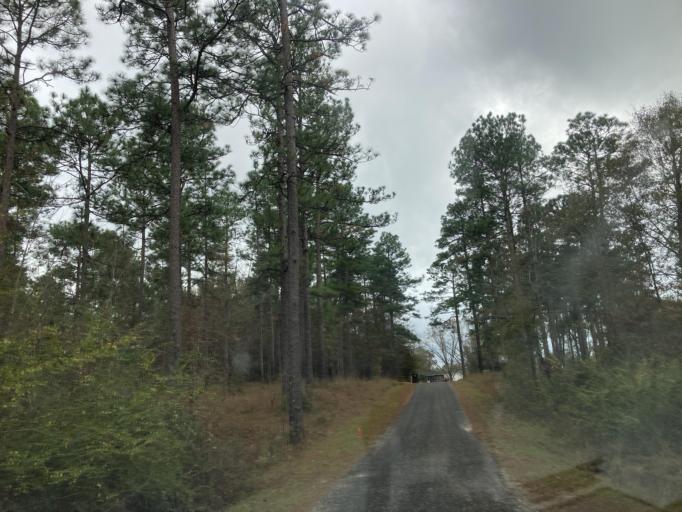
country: US
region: Mississippi
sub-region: Lamar County
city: Lumberton
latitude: 31.0956
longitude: -89.5325
